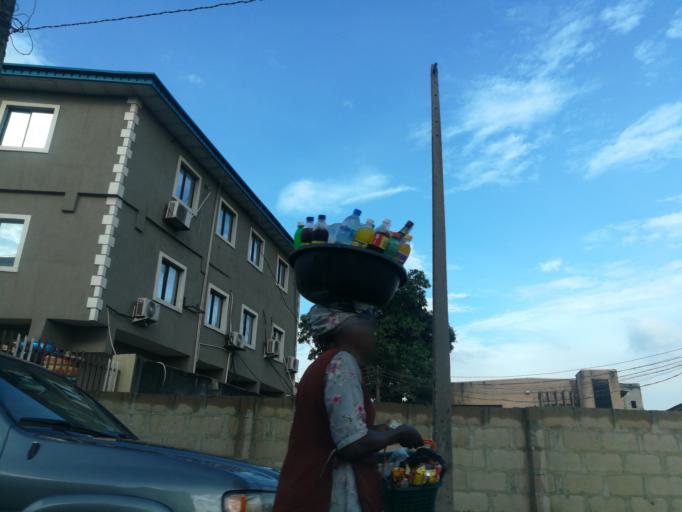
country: NG
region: Lagos
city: Ikeja
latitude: 6.5954
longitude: 3.3441
